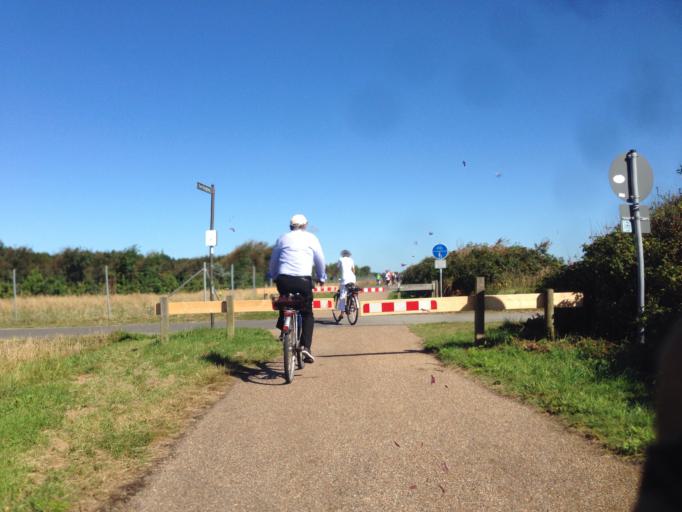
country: DE
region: Schleswig-Holstein
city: Tinnum
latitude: 54.9426
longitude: 8.3324
